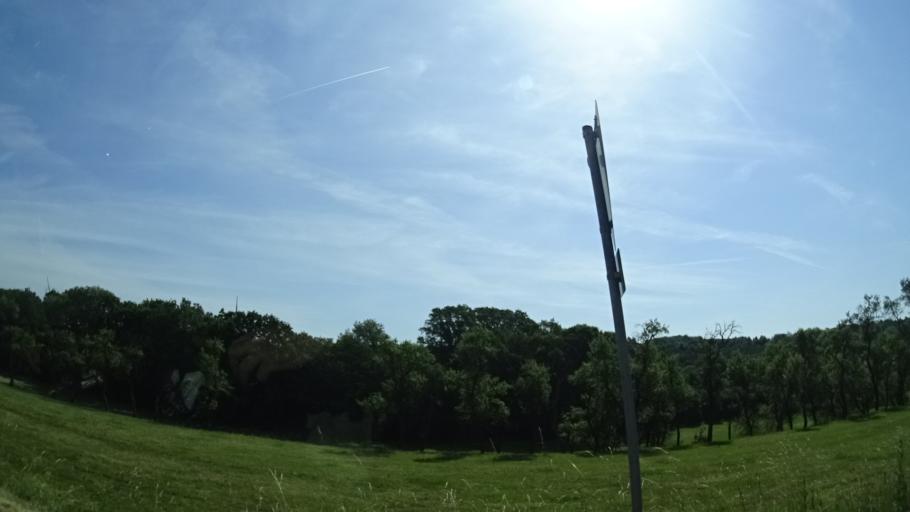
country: DE
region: Hesse
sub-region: Regierungsbezirk Giessen
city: Rauschenberg
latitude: 50.8630
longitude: 8.8673
